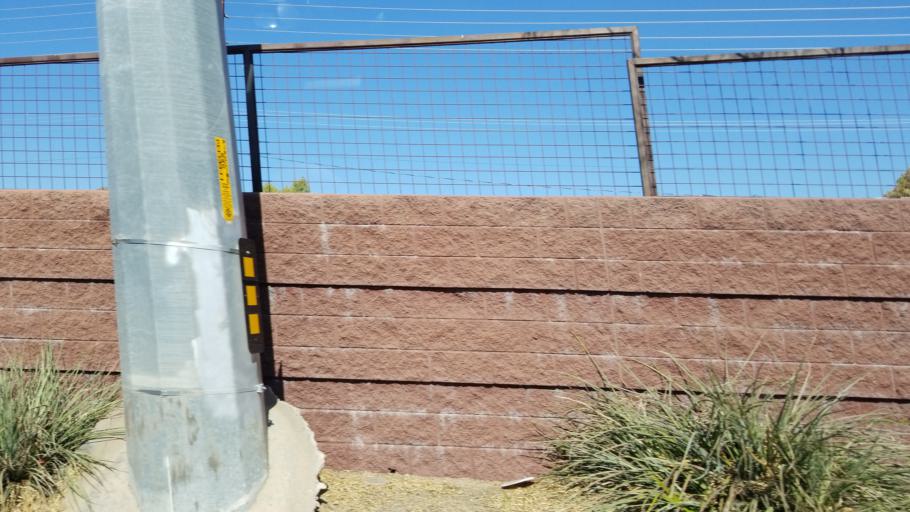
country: US
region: Arizona
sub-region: Maricopa County
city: Paradise Valley
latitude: 33.4900
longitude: -111.9489
